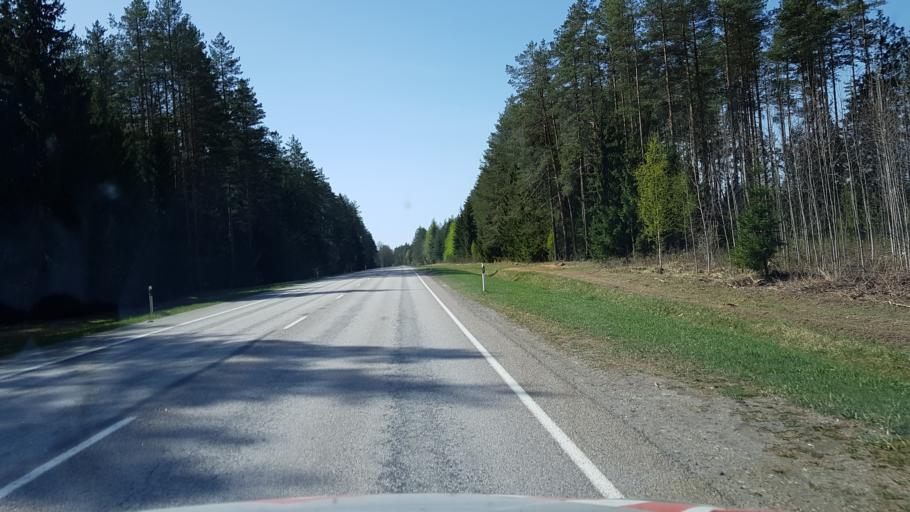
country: EE
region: Valgamaa
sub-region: Valga linn
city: Valga
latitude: 57.8221
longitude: 26.0501
